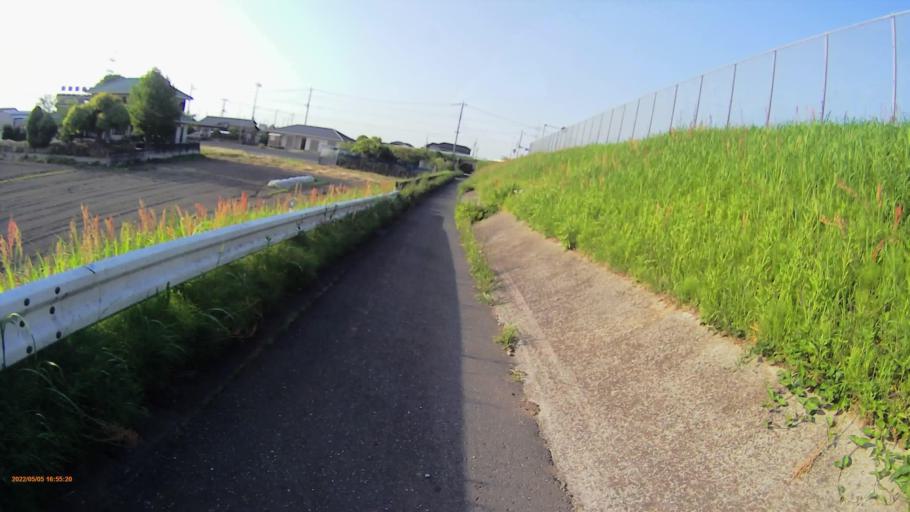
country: JP
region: Saitama
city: Kurihashi
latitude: 36.1083
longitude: 139.7234
